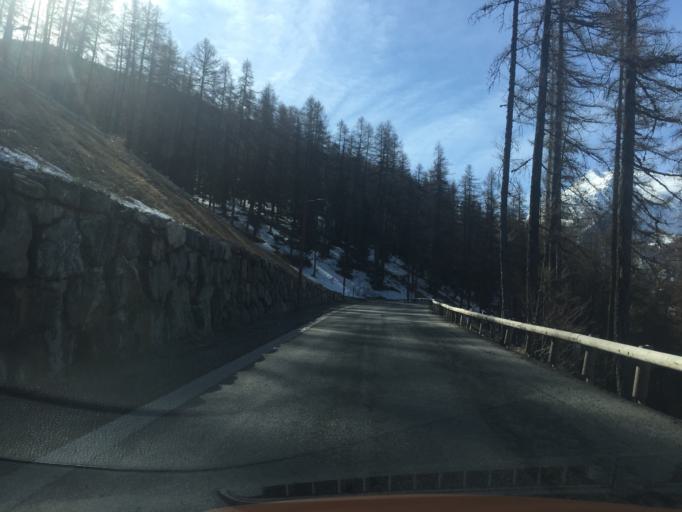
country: FR
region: Provence-Alpes-Cote d'Azur
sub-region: Departement des Hautes-Alpes
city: Embrun
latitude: 44.4820
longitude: 6.5519
